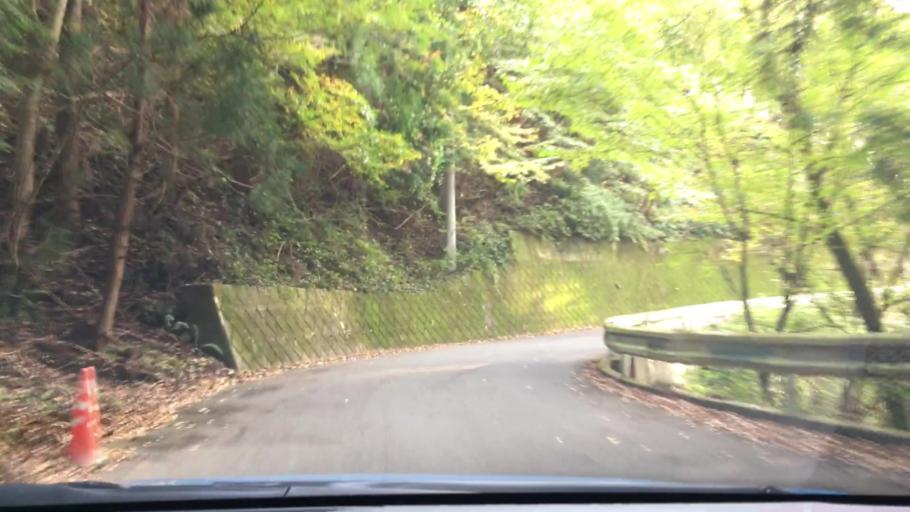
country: JP
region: Yamanashi
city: Uenohara
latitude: 35.5603
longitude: 139.1548
